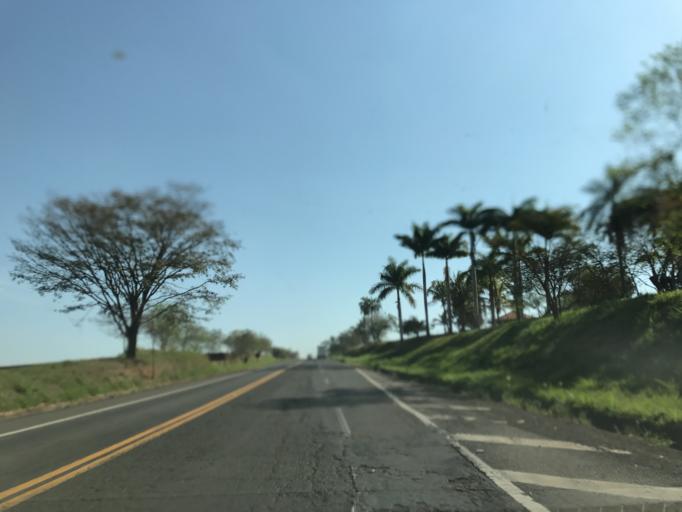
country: BR
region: Sao Paulo
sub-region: Penapolis
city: Penapolis
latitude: -21.4593
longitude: -50.1724
